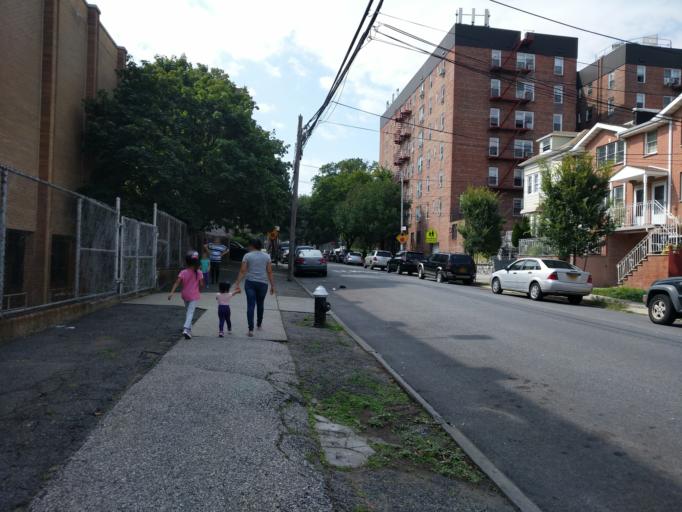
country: US
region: New York
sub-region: Queens County
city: Long Island City
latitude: 40.7470
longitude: -73.9077
